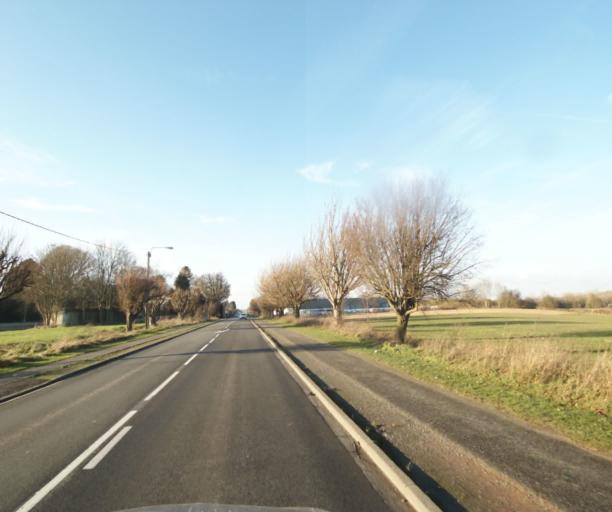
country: FR
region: Nord-Pas-de-Calais
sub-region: Departement du Nord
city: Saultain
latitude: 50.3388
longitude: 3.5709
